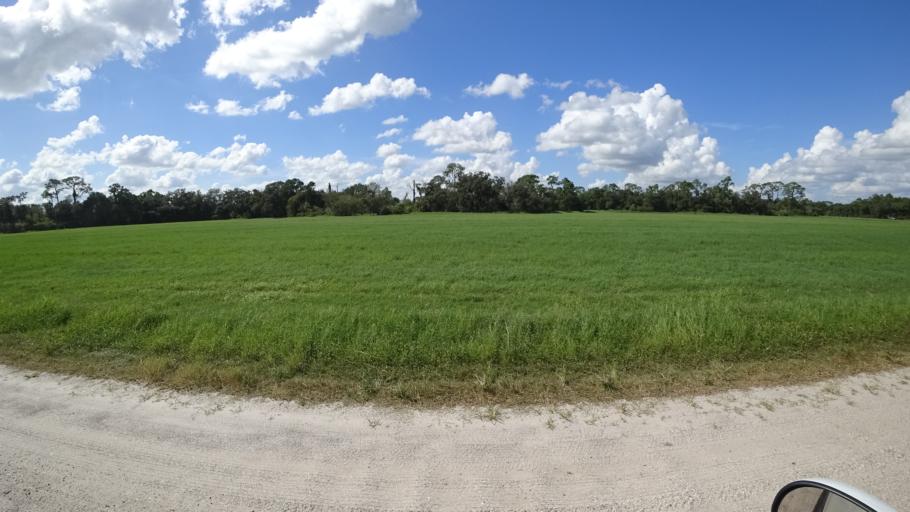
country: US
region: Florida
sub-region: DeSoto County
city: Arcadia
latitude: 27.3217
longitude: -82.1244
